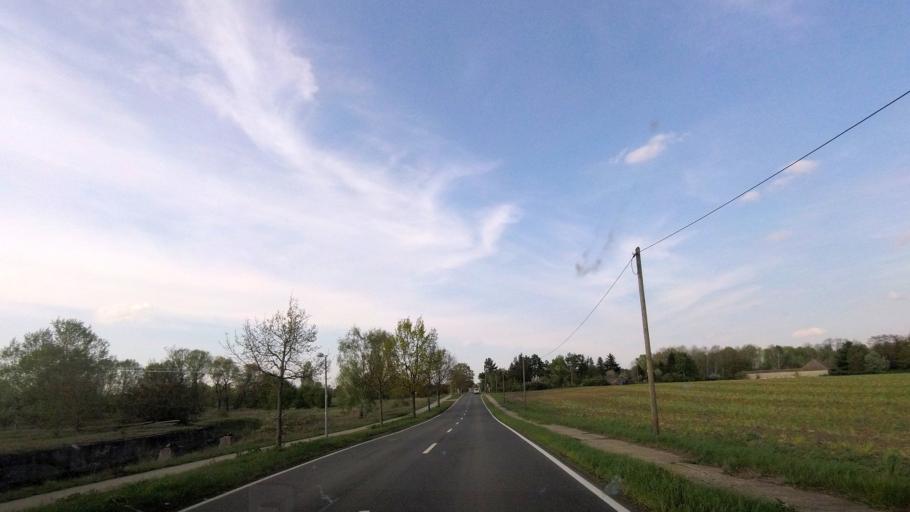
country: DE
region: Saxony-Anhalt
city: Abtsdorf
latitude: 51.8677
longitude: 12.6937
